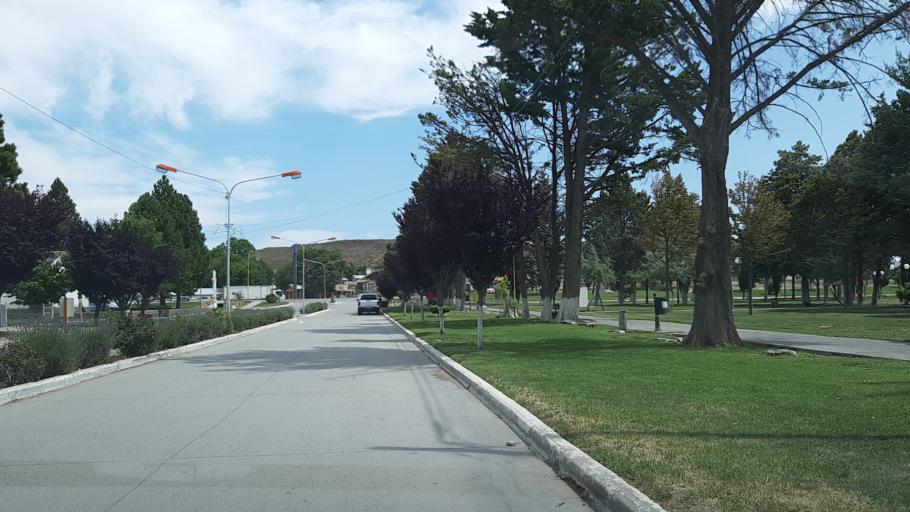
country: AR
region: Neuquen
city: Piedra del Aguila
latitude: -40.0492
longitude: -70.0752
